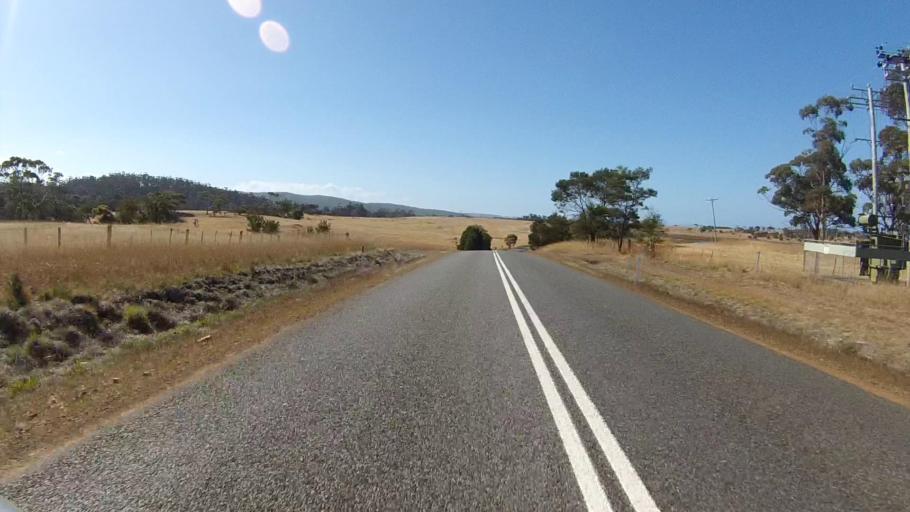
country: AU
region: Tasmania
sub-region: Sorell
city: Sorell
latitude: -42.2828
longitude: 147.9985
